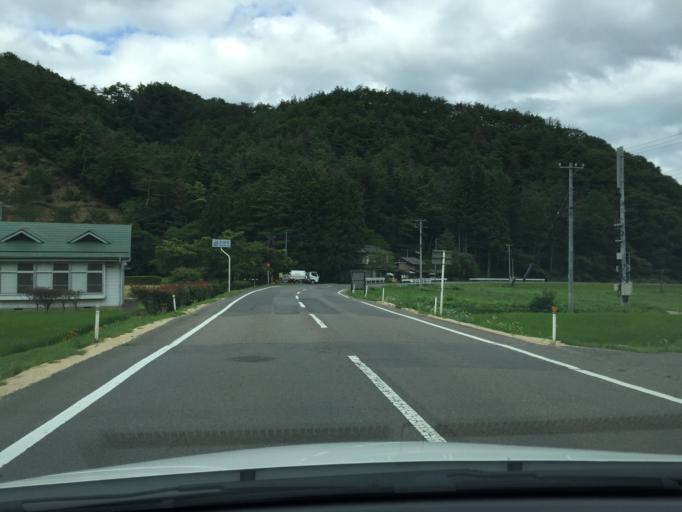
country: JP
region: Fukushima
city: Sukagawa
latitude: 37.1850
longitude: 140.1848
